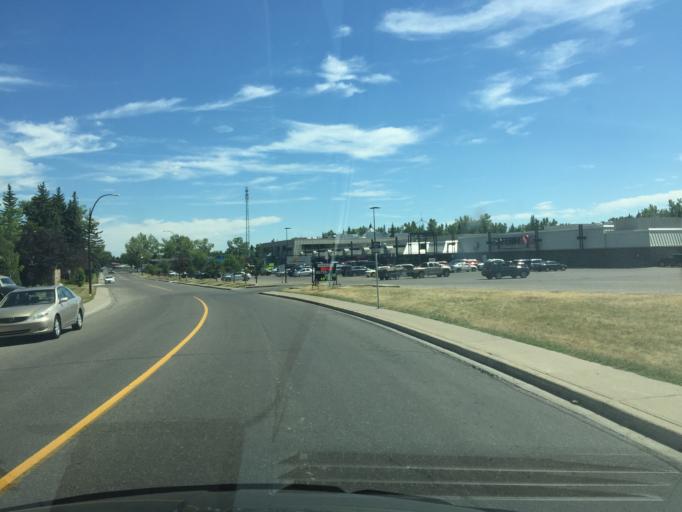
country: CA
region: Alberta
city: Calgary
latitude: 50.9438
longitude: -114.0482
